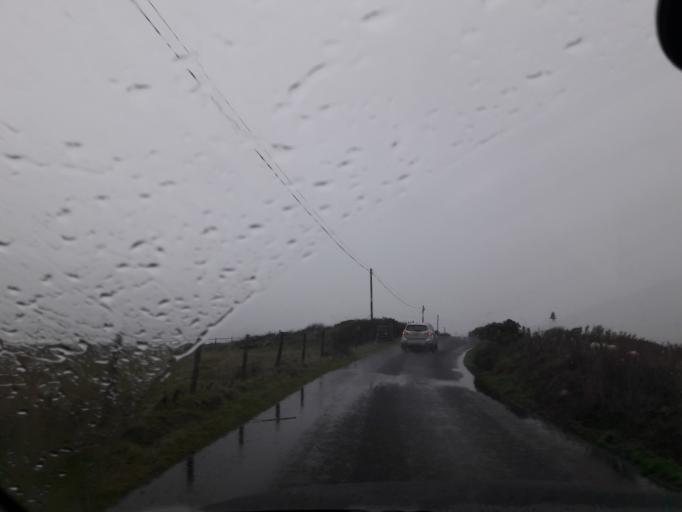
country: IE
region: Ulster
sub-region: County Donegal
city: Buncrana
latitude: 55.2736
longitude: -7.6386
